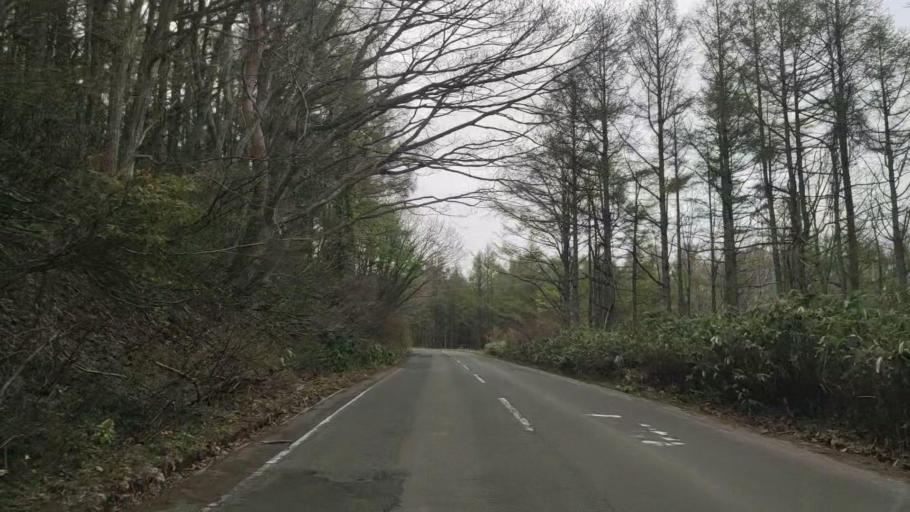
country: JP
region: Aomori
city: Aomori Shi
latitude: 40.7296
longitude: 140.8457
